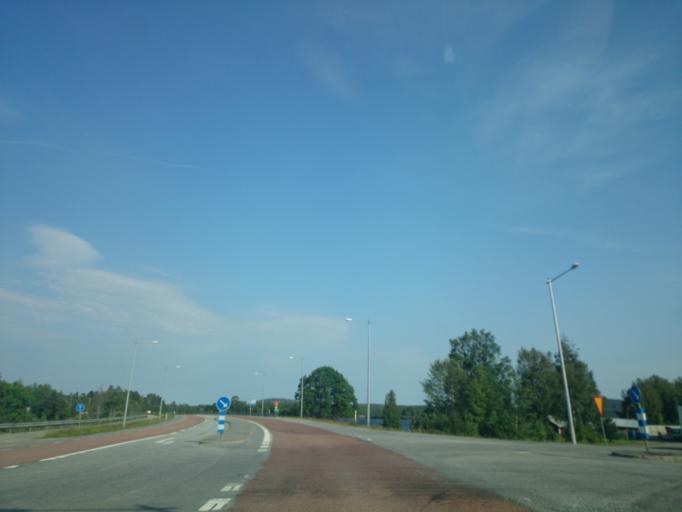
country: SE
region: Jaemtland
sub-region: Braecke Kommun
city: Braecke
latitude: 62.9184
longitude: 15.2395
